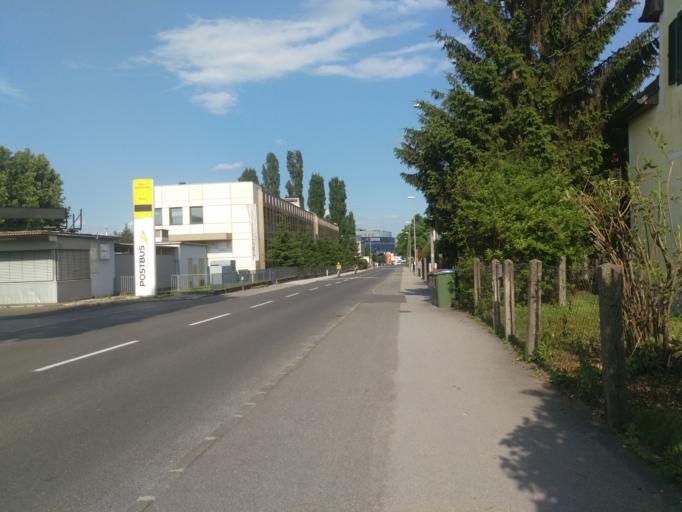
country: AT
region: Styria
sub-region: Graz Stadt
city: Wetzelsdorf
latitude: 47.0592
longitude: 15.4228
